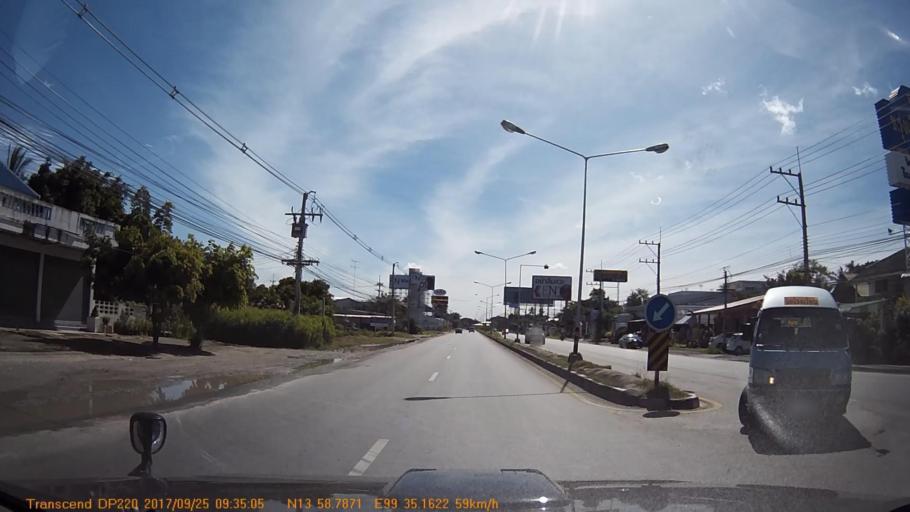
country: TH
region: Kanchanaburi
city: Kanchanaburi
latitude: 13.9798
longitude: 99.5862
